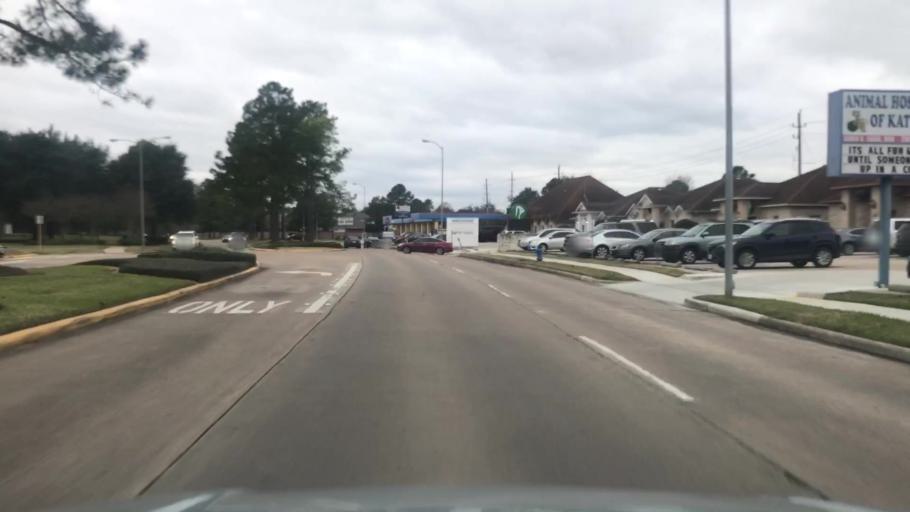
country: US
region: Texas
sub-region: Fort Bend County
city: Cinco Ranch
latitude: 29.7590
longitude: -95.7572
